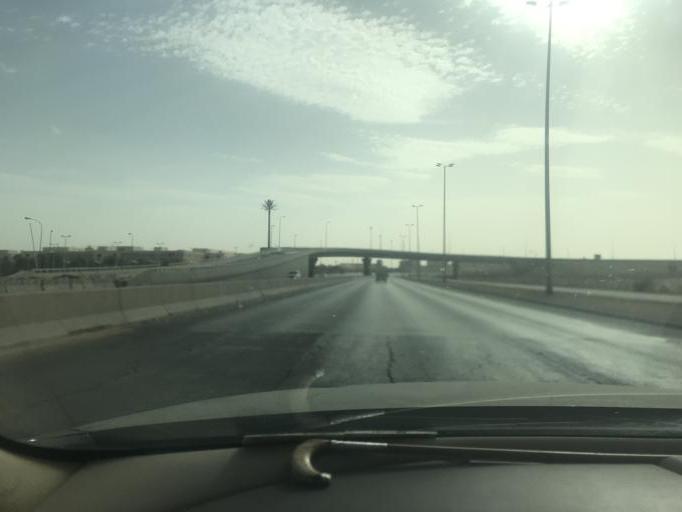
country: SA
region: Ar Riyad
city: Riyadh
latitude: 24.8220
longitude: 46.7114
